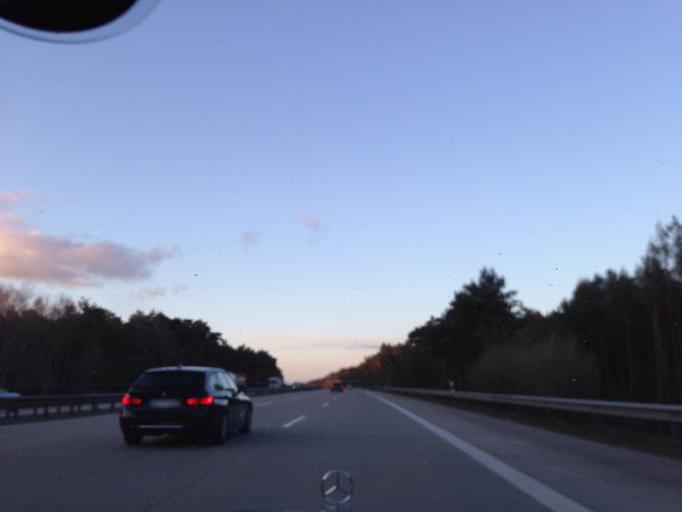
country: DE
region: Lower Saxony
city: Egestorf
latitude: 53.1665
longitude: 10.0707
